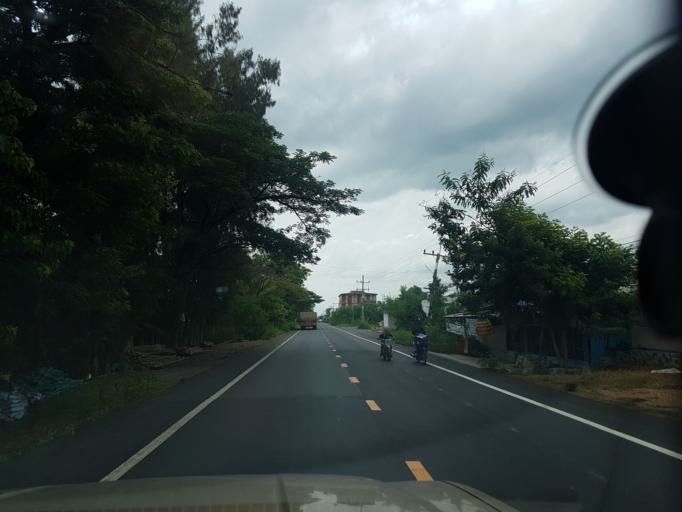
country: TH
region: Sara Buri
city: Nong Khae
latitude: 14.2833
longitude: 100.8917
